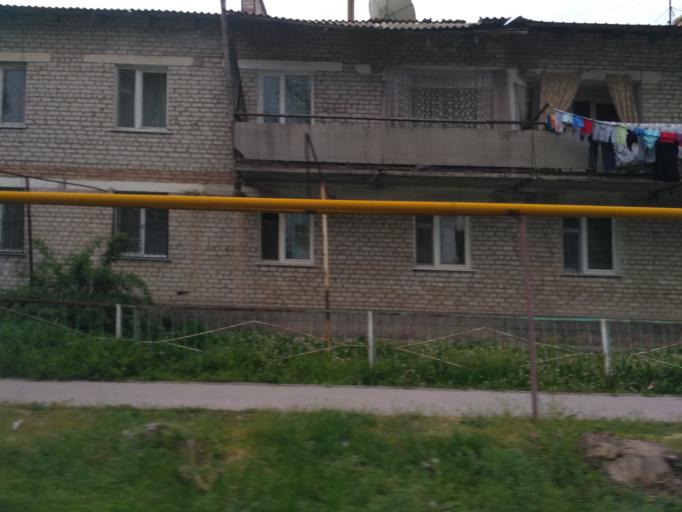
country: KZ
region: Almaty Oblysy
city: Burunday
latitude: 43.4576
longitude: 76.7248
